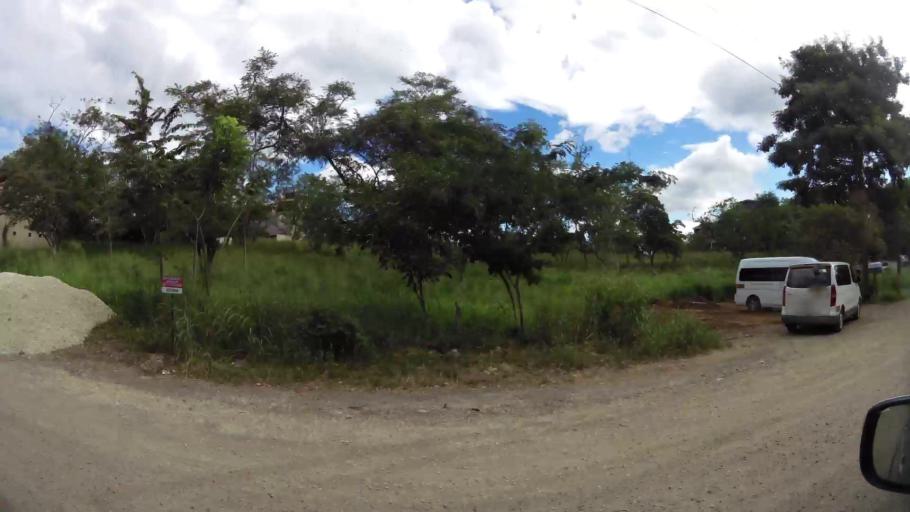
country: CR
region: Guanacaste
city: Santa Cruz
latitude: 10.2870
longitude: -85.8504
